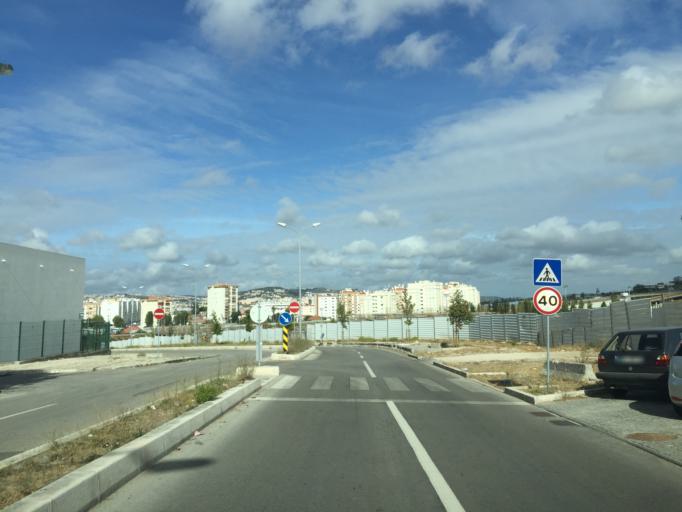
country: PT
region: Lisbon
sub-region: Odivelas
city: Olival do Basto
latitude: 38.7781
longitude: -9.1528
